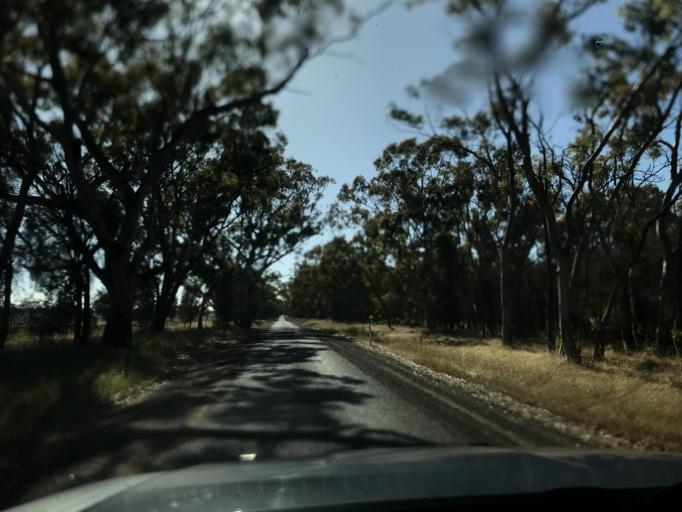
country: AU
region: Victoria
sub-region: Horsham
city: Horsham
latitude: -37.0076
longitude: 141.6466
